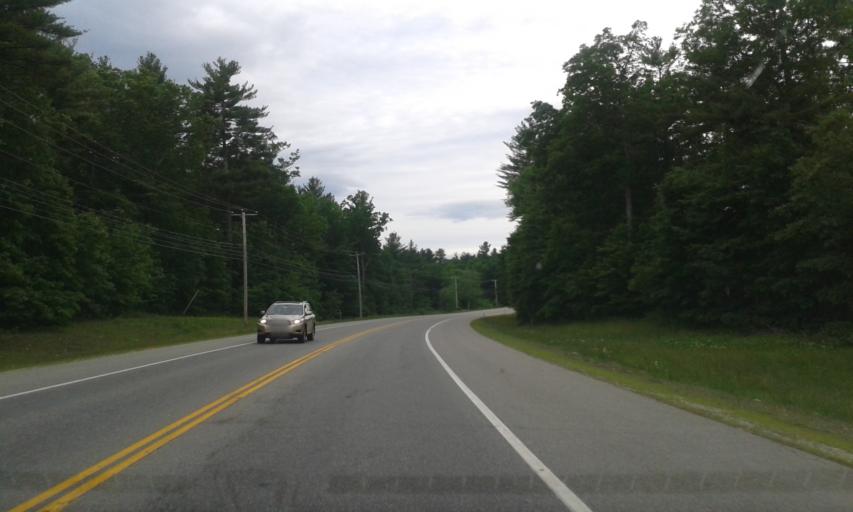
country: US
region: New Hampshire
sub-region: Hillsborough County
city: Litchfield
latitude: 42.8120
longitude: -71.5207
